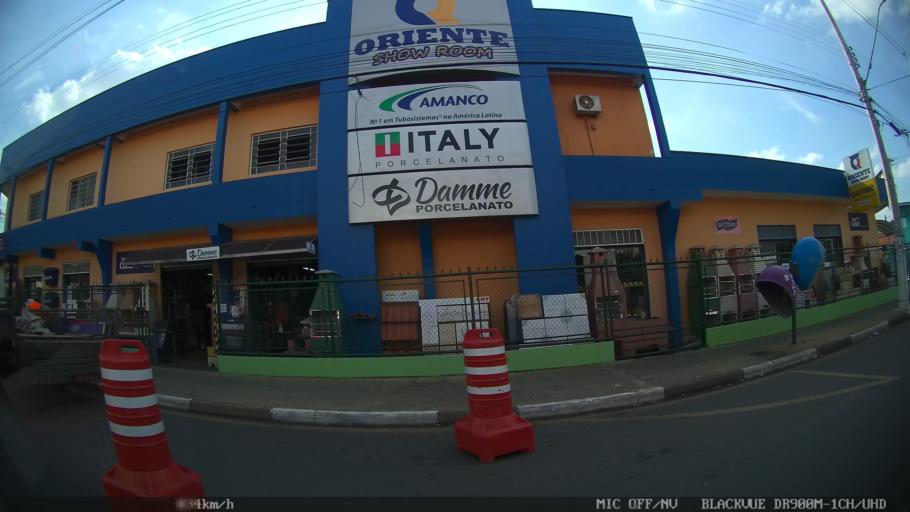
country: BR
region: Sao Paulo
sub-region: Hortolandia
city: Hortolandia
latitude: -22.9031
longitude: -47.2429
